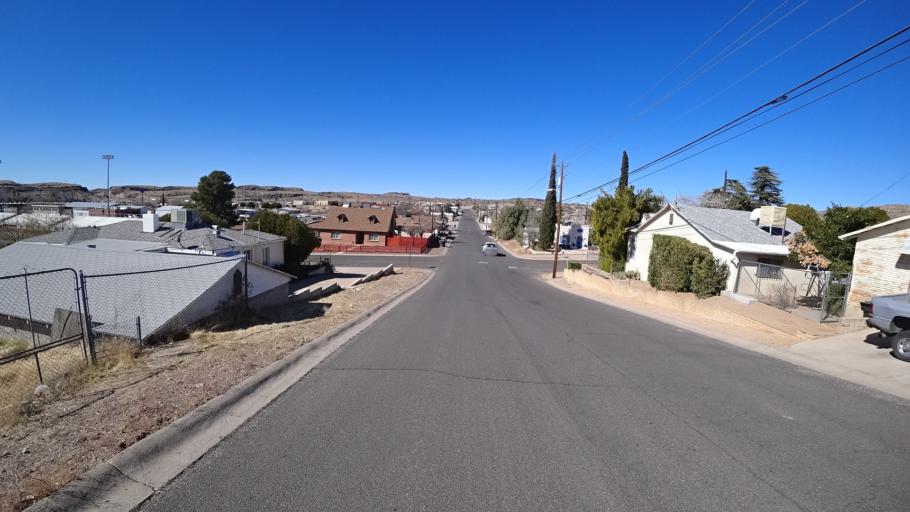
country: US
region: Arizona
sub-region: Mohave County
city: Kingman
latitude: 35.1945
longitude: -114.0583
